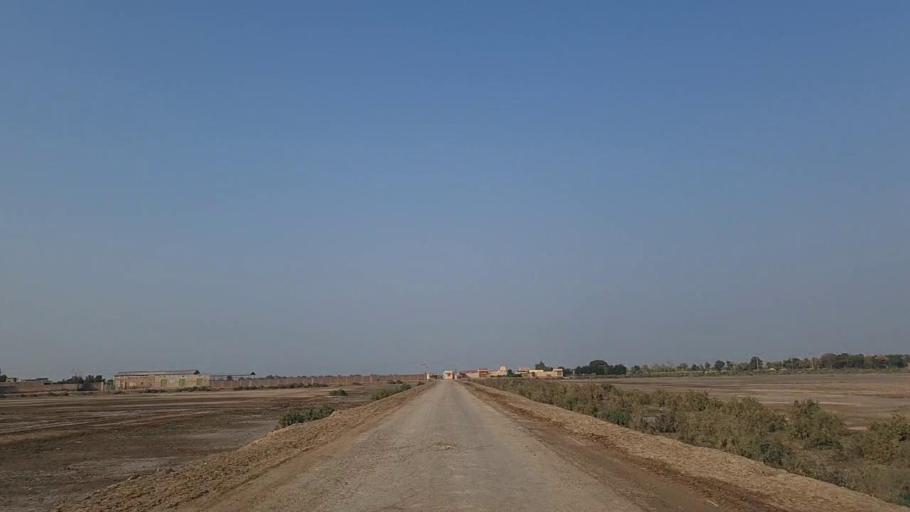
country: PK
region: Sindh
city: Jam Sahib
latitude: 26.2874
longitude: 68.6086
